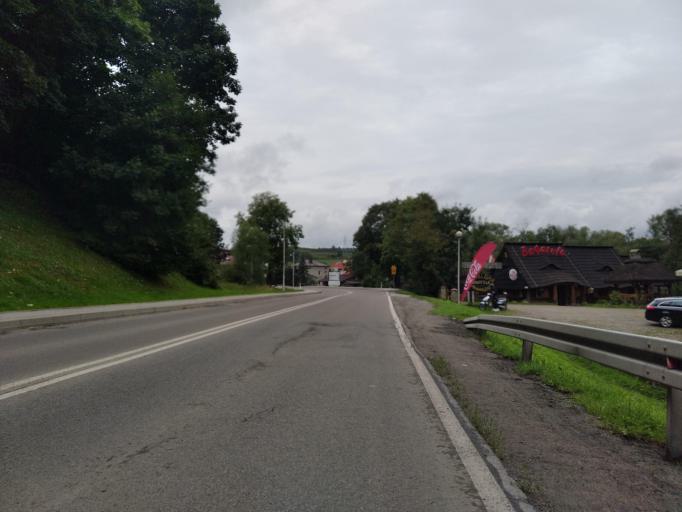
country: PL
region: Subcarpathian Voivodeship
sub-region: Powiat przemyski
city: Bircza
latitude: 49.6918
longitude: 22.4826
